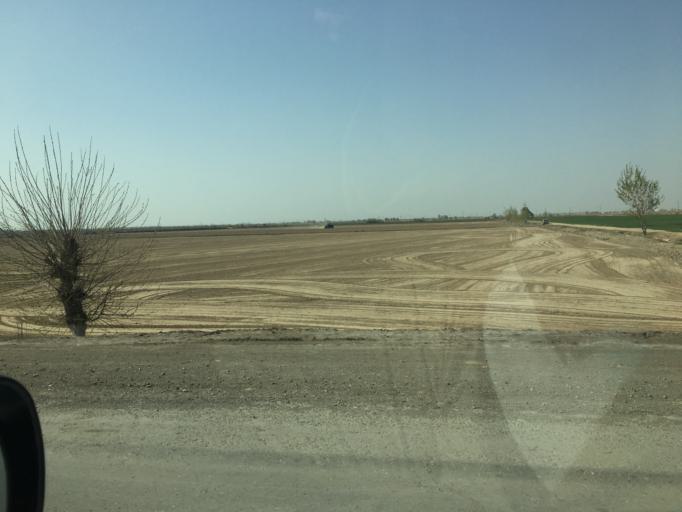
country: TM
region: Lebap
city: Turkmenabat
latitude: 39.0063
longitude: 63.6097
